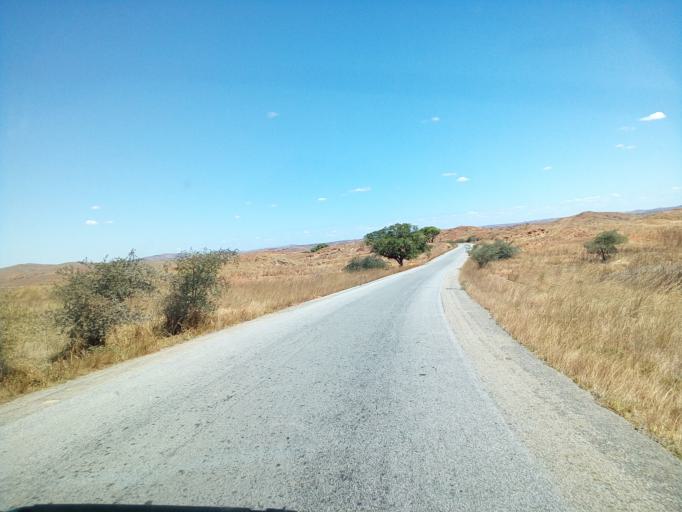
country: MG
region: Betsiboka
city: Maevatanana
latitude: -17.1072
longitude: 46.8113
